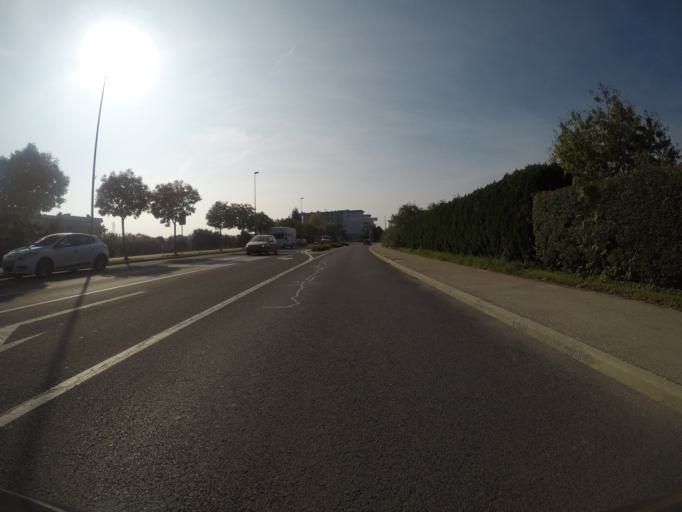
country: SI
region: Kamnik
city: Kamnik
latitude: 46.2158
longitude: 14.6025
